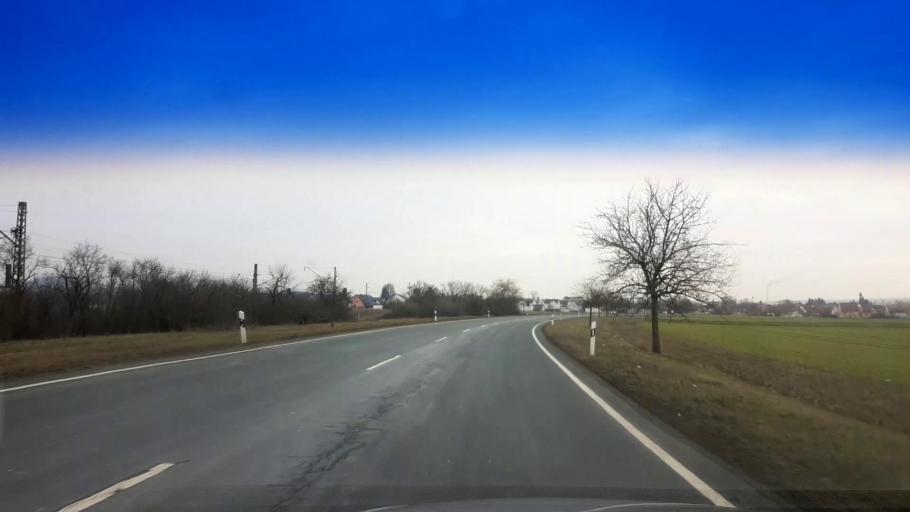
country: DE
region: Bavaria
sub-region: Upper Franconia
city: Altendorf
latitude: 49.8063
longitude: 11.0053
